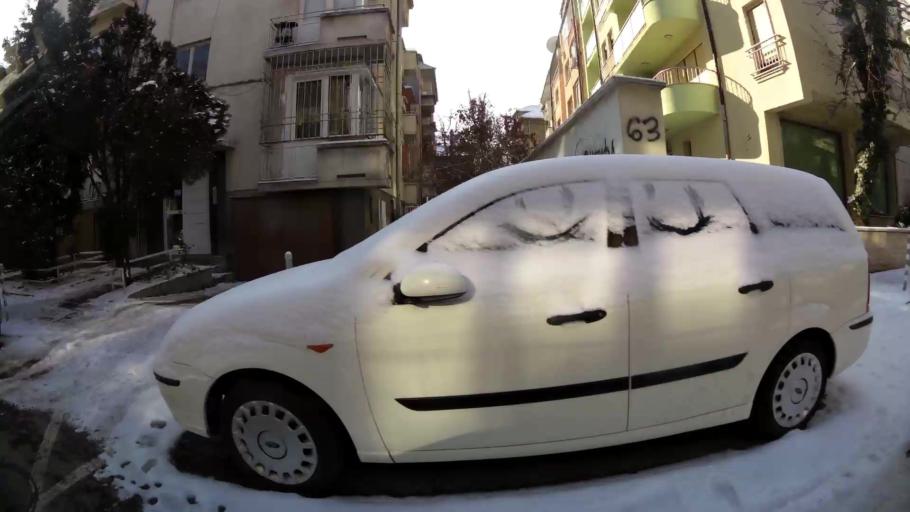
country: BG
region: Sofia-Capital
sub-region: Stolichna Obshtina
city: Sofia
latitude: 42.6813
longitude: 23.3278
